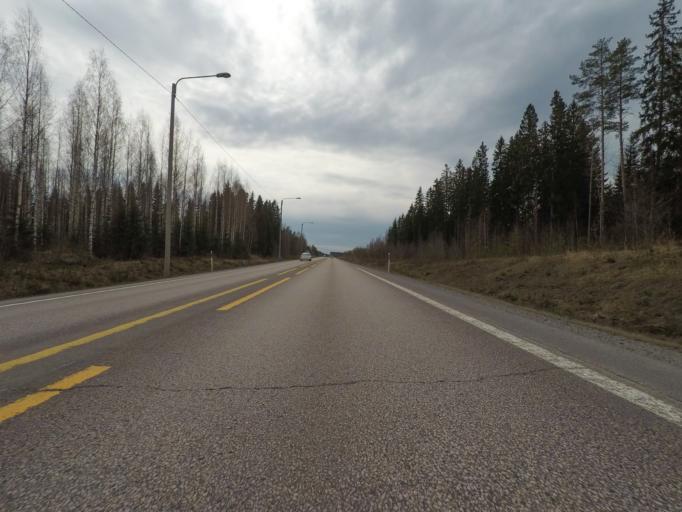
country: FI
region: Paijanne Tavastia
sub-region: Lahti
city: Hartola
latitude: 61.5177
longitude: 25.9974
